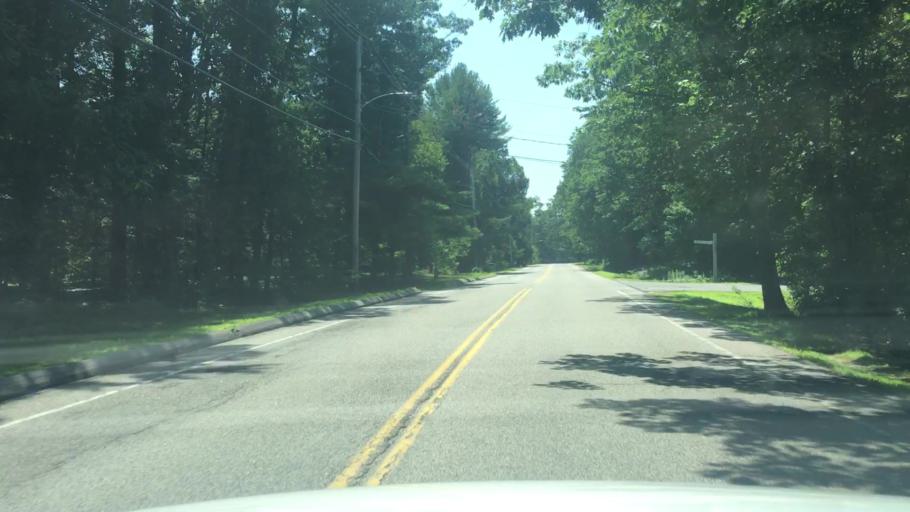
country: US
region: Maine
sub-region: Cumberland County
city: Cumberland Center
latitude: 43.7650
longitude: -70.2739
